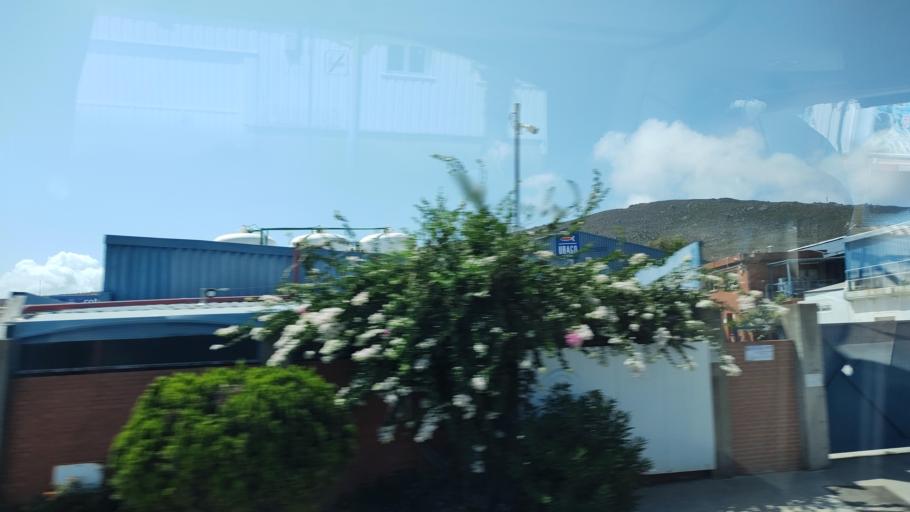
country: ES
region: Andalusia
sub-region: Provincia de Cadiz
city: La Linea de la Concepcion
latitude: 36.1870
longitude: -5.3494
